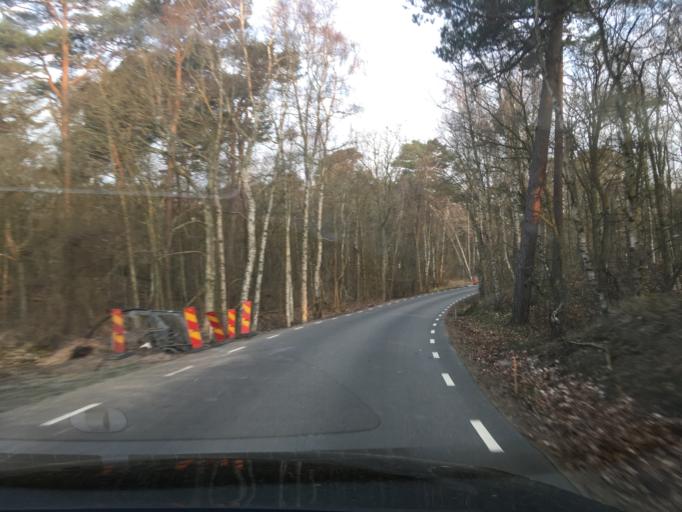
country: SE
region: Skane
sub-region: Simrishamns Kommun
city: Simrishamn
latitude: 55.3886
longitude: 14.1909
